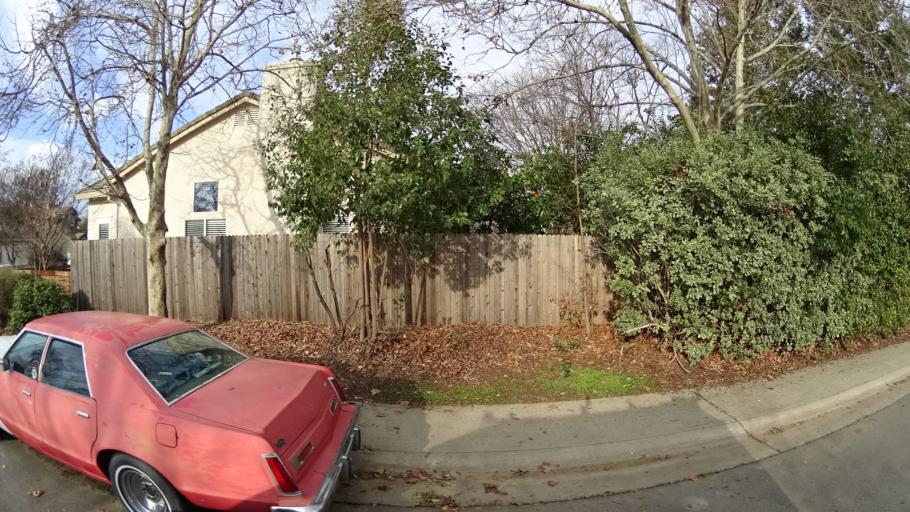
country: US
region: California
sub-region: Yolo County
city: Davis
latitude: 38.5592
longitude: -121.7106
